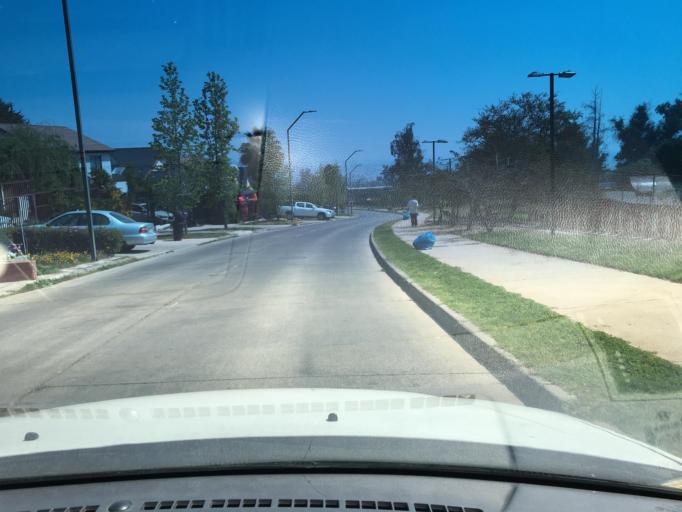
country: CL
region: Santiago Metropolitan
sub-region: Provincia de Santiago
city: Villa Presidente Frei, Nunoa, Santiago, Chile
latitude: -33.5104
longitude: -70.5292
